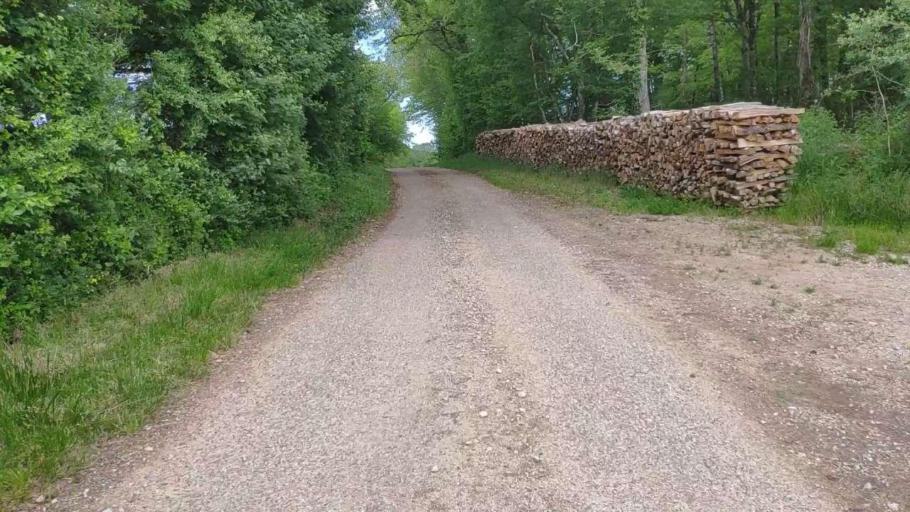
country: FR
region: Franche-Comte
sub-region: Departement du Jura
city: Poligny
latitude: 46.7706
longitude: 5.6551
